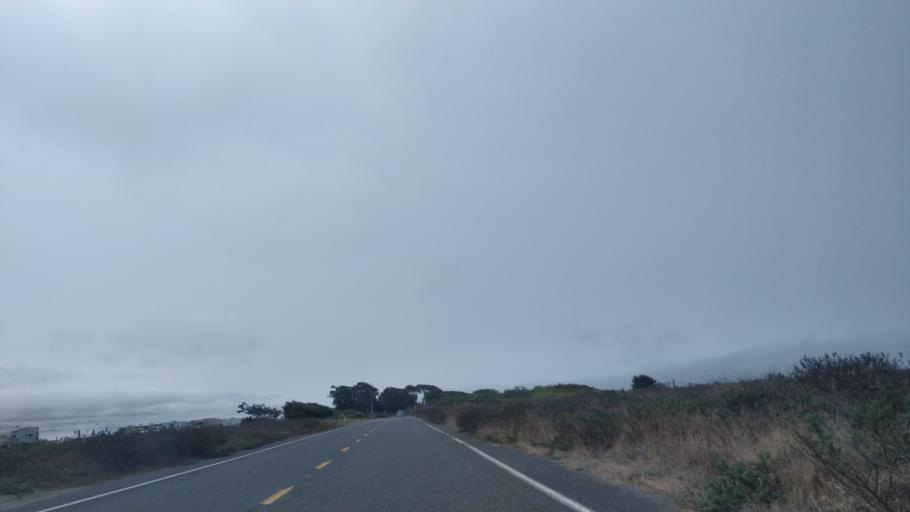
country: US
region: California
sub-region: Humboldt County
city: Bayview
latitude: 40.7744
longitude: -124.2123
